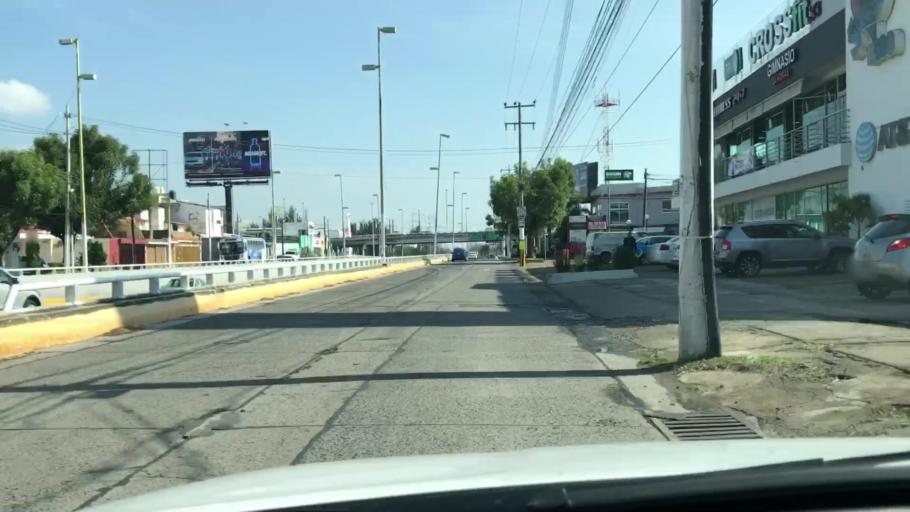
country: MX
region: Jalisco
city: Guadalajara
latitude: 20.6768
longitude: -103.4219
